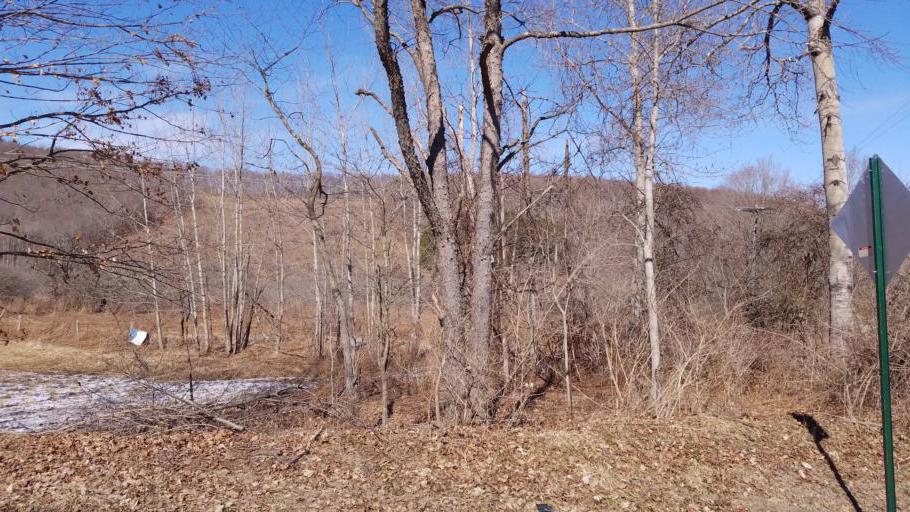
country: US
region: New York
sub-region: Allegany County
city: Wellsville
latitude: 42.0227
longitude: -77.9246
